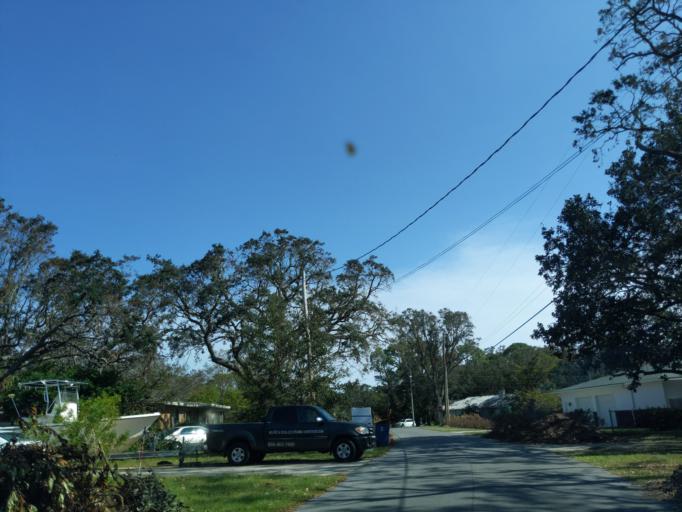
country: US
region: Florida
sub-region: Santa Rosa County
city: Gulf Breeze
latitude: 30.3567
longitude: -87.1924
